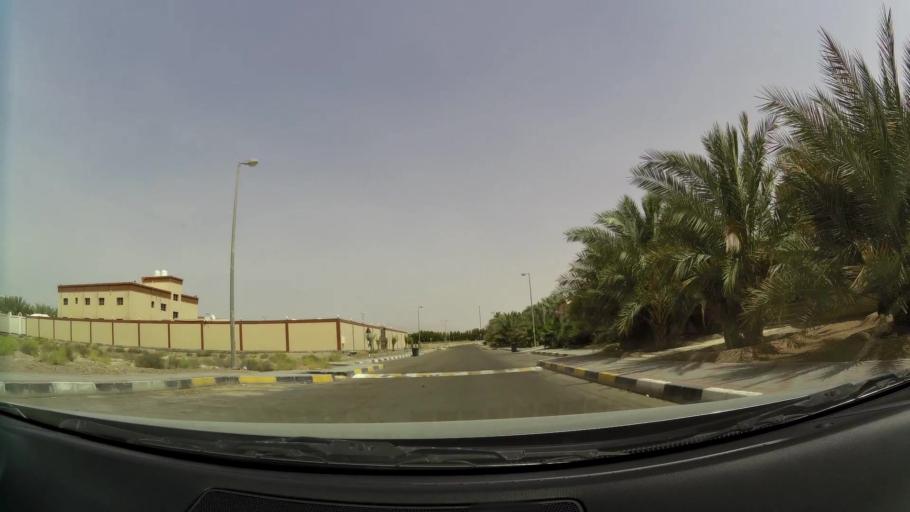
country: AE
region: Abu Dhabi
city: Al Ain
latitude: 24.1511
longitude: 55.6543
